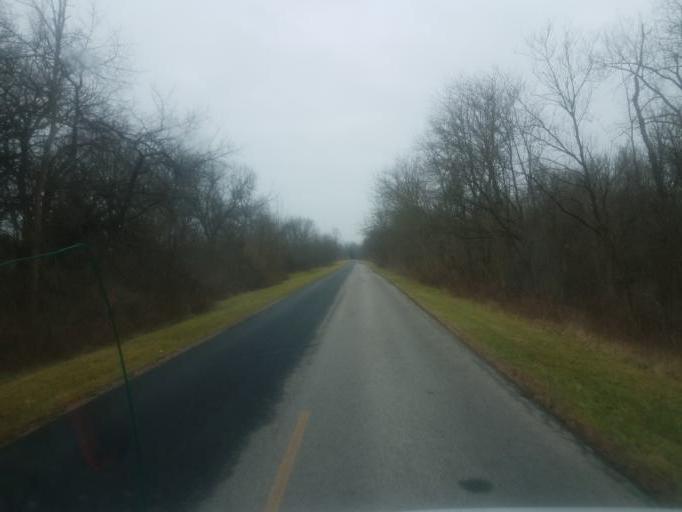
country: US
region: Ohio
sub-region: Delaware County
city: Sunbury
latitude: 40.2422
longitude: -82.8925
